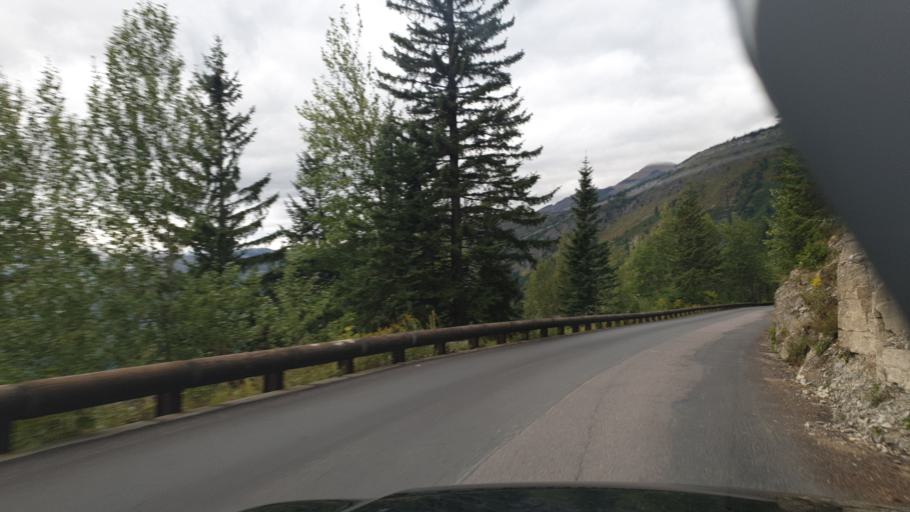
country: US
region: Montana
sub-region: Flathead County
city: Columbia Falls
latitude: 48.7260
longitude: -113.7421
